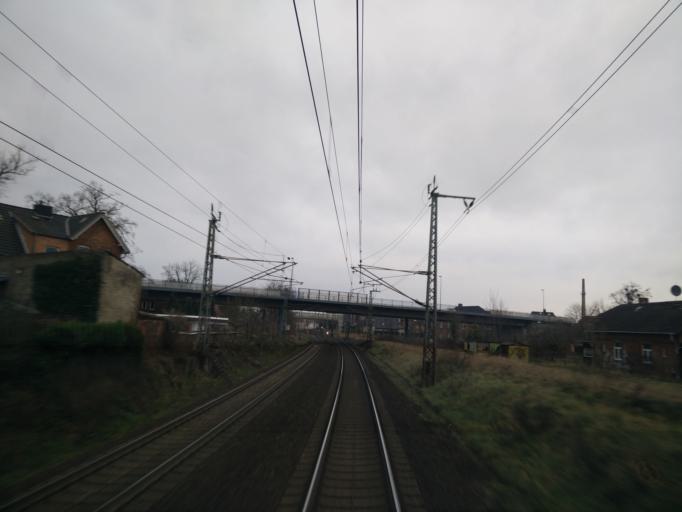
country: DE
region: Mecklenburg-Vorpommern
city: Ludwigslust
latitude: 53.3295
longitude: 11.5033
